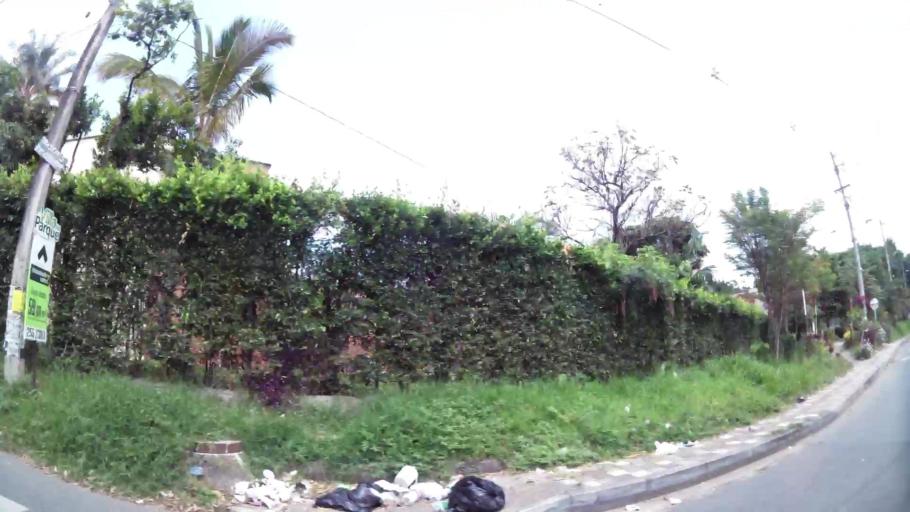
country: CO
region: Antioquia
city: Itagui
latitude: 6.1915
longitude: -75.5973
